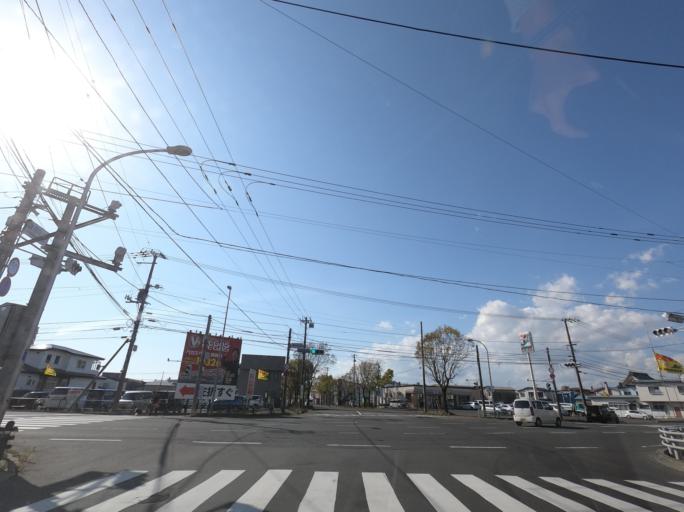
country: JP
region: Hokkaido
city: Kushiro
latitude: 42.9891
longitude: 144.3763
